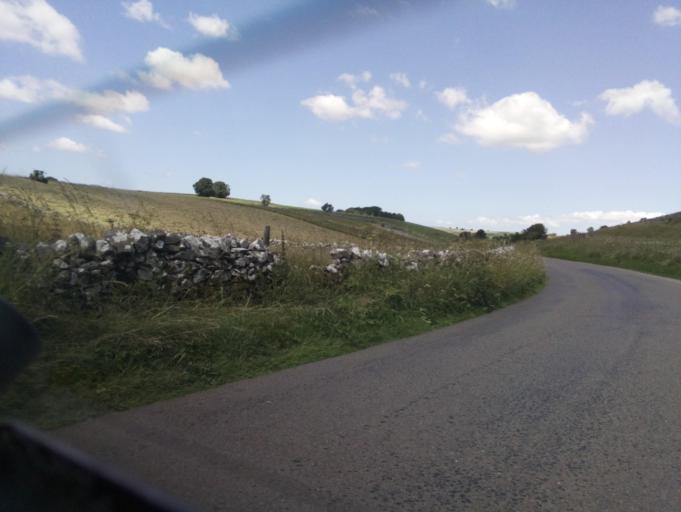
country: GB
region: England
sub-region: Derbyshire
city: Tideswell
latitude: 53.2015
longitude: -1.7768
